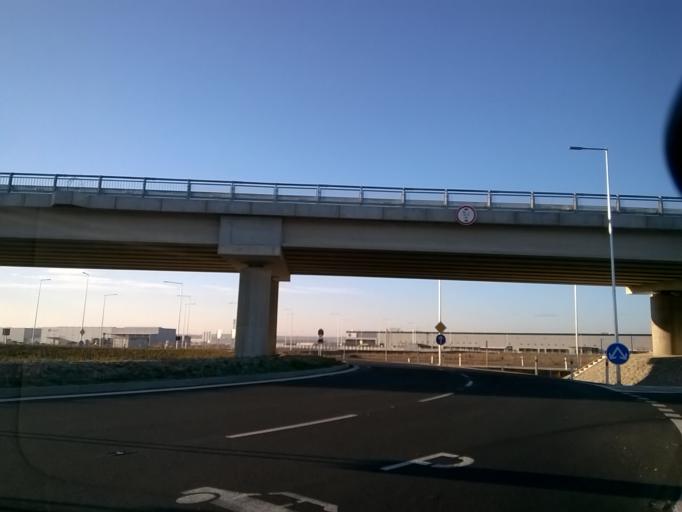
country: SK
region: Nitriansky
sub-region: Okres Nitra
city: Nitra
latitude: 48.3416
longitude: 18.0595
